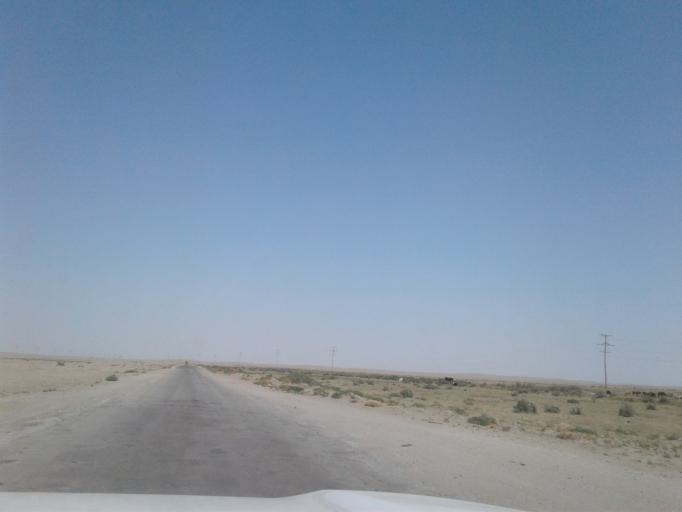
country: TM
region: Balkan
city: Gumdag
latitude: 38.3532
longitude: 54.3727
